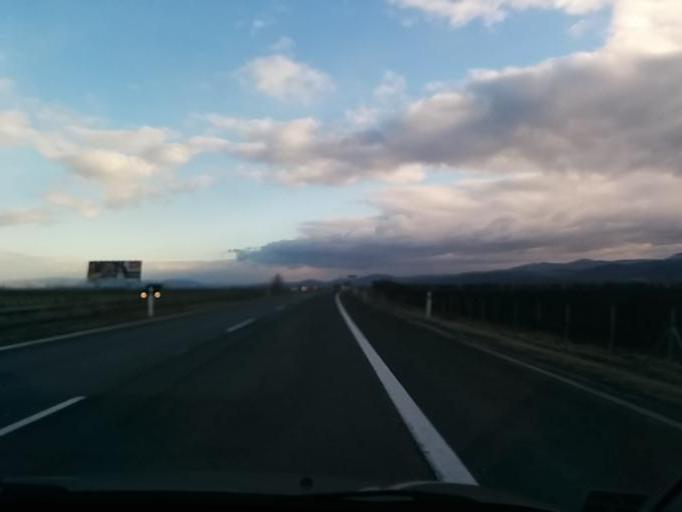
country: SK
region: Trnavsky
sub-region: Okres Trnava
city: Piestany
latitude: 48.6362
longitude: 17.8119
